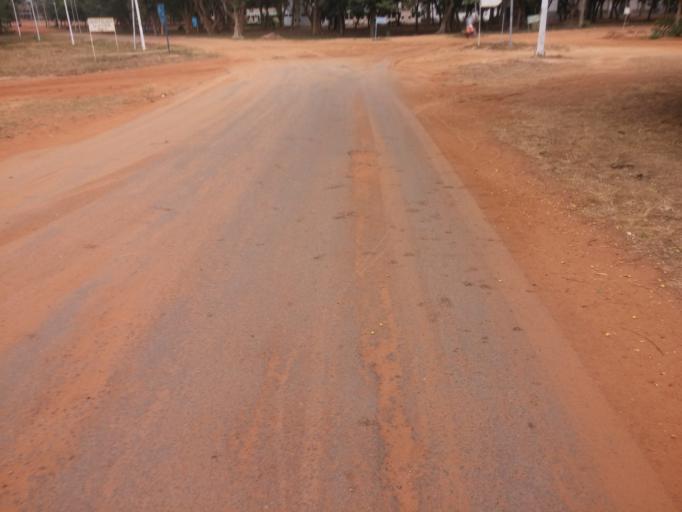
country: TG
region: Maritime
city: Lome
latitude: 6.1735
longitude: 1.2156
